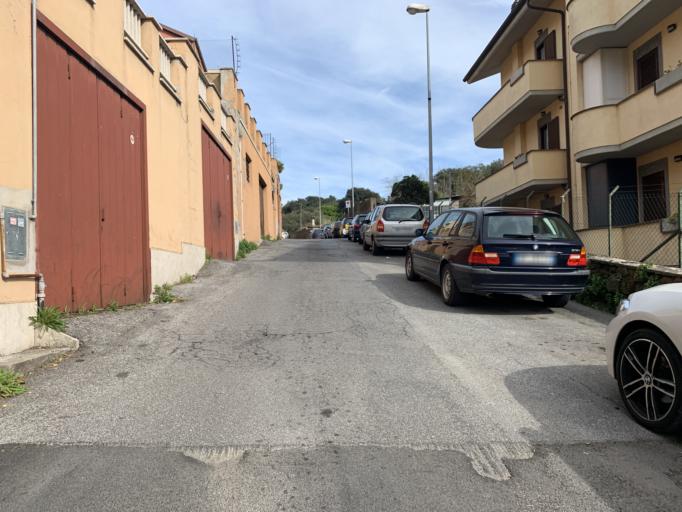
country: IT
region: Latium
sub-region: Citta metropolitana di Roma Capitale
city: Grottaferrata
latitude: 41.7679
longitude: 12.6654
